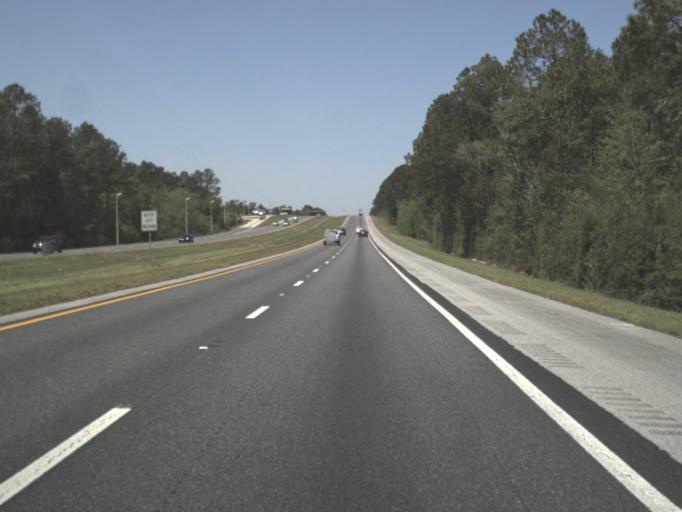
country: US
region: Florida
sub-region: Escambia County
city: Cantonment
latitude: 30.5670
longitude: -87.3904
